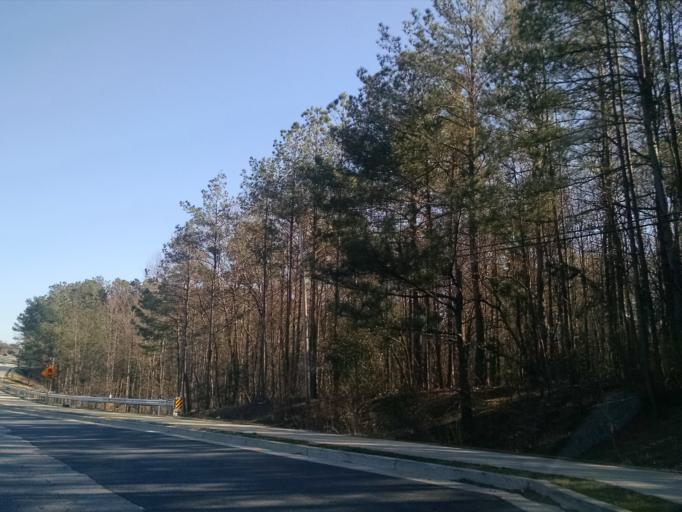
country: US
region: Georgia
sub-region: Gwinnett County
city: Suwanee
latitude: 34.0610
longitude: -84.0721
